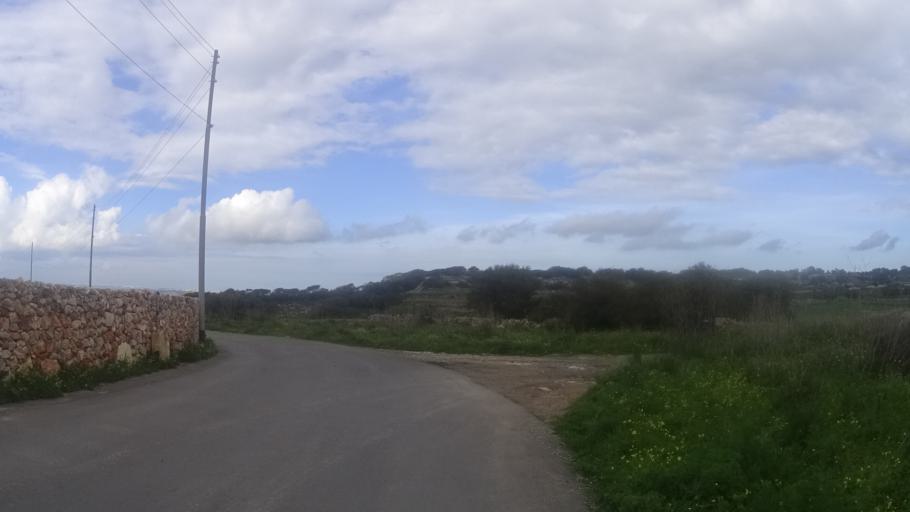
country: MT
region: L-Imtarfa
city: Imtarfa
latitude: 35.9021
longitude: 14.3791
